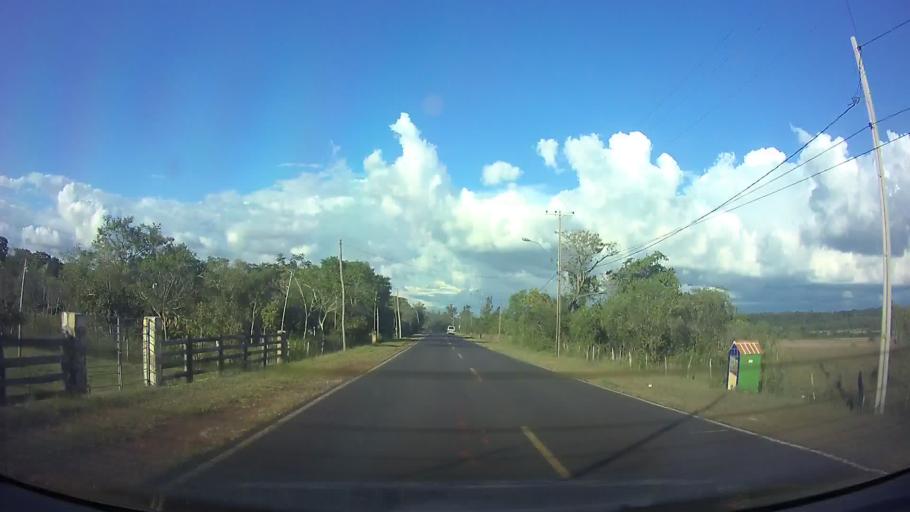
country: PY
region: Cordillera
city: Emboscada
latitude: -25.1623
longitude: -57.2665
